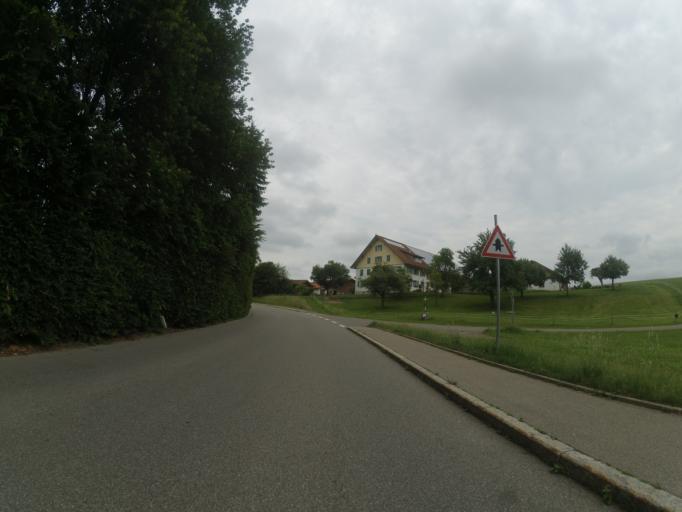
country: DE
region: Bavaria
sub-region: Swabia
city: Gestratz
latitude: 47.6891
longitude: 9.9660
